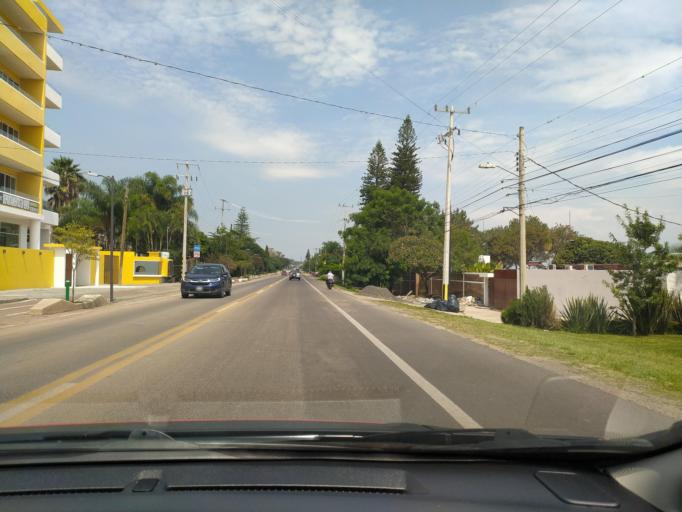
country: MX
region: Jalisco
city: San Juan Cosala
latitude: 20.2904
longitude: -103.3566
